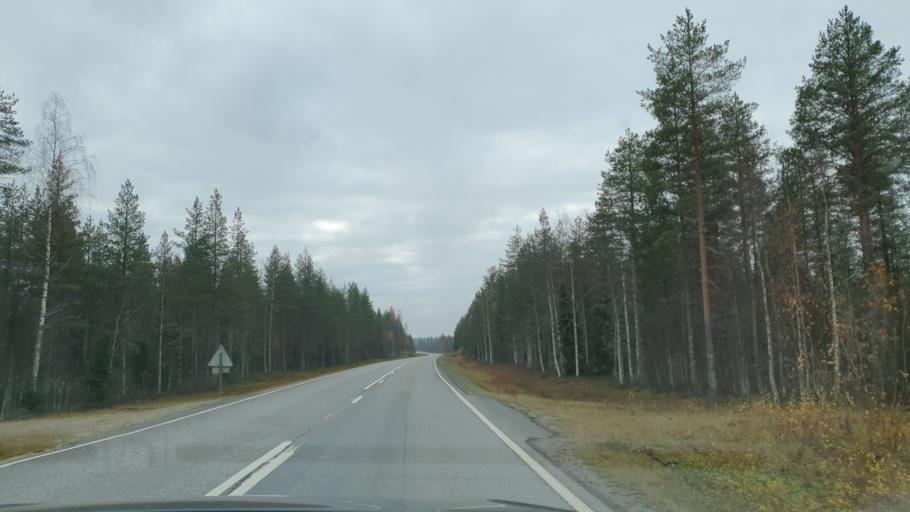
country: FI
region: Lapland
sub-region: Rovaniemi
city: Ranua
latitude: 66.0341
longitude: 26.3334
